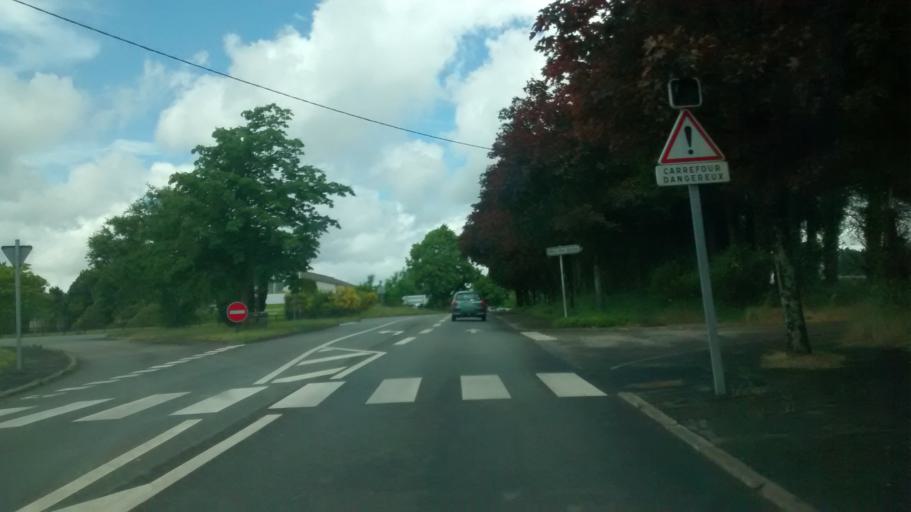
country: FR
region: Brittany
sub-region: Departement du Morbihan
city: La Gacilly
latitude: 47.7722
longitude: -2.1312
